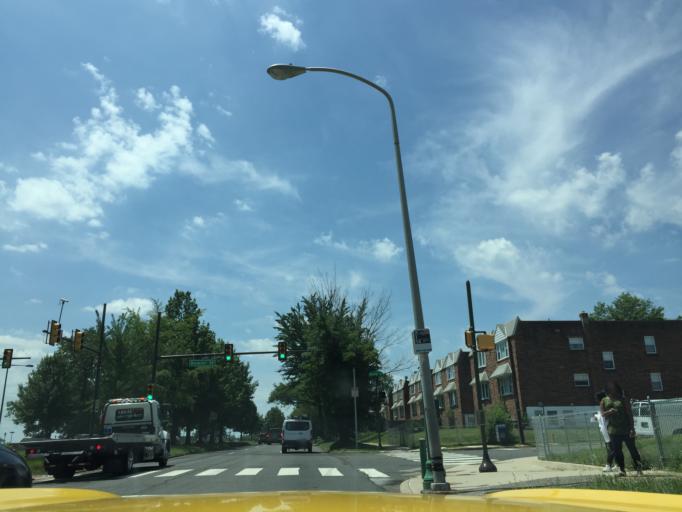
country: US
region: Pennsylvania
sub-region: Bucks County
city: Feasterville
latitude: 40.0865
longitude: -75.0237
